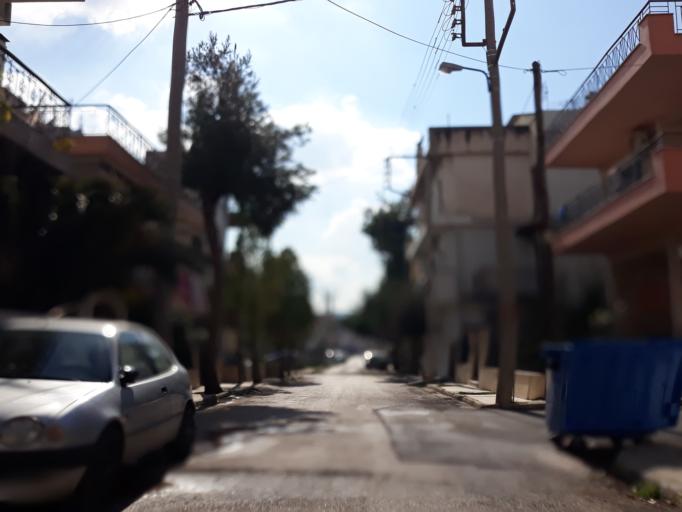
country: GR
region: Attica
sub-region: Nomarchia Dytikis Attikis
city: Ano Liosia
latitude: 38.0891
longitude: 23.7066
